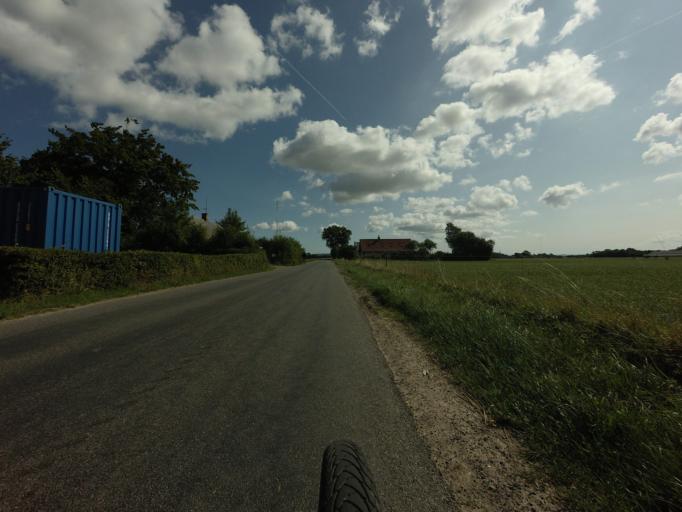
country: DK
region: Zealand
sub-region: Vordingborg Kommune
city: Stege
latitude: 54.9734
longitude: 12.3617
